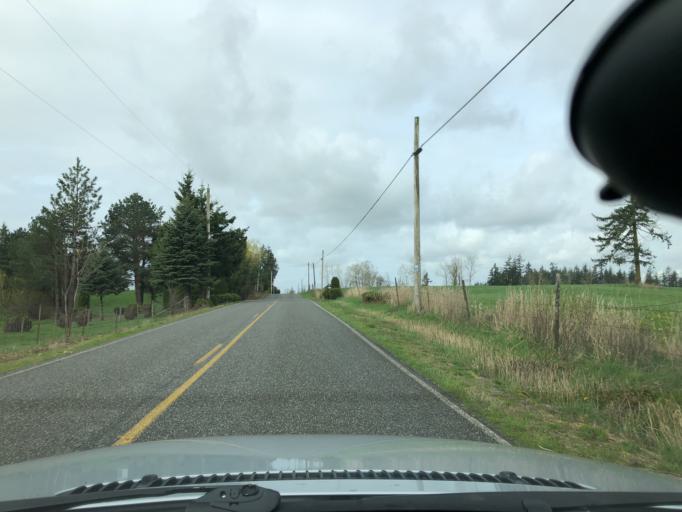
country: CA
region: British Columbia
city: Langley
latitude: 48.9795
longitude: -122.5692
